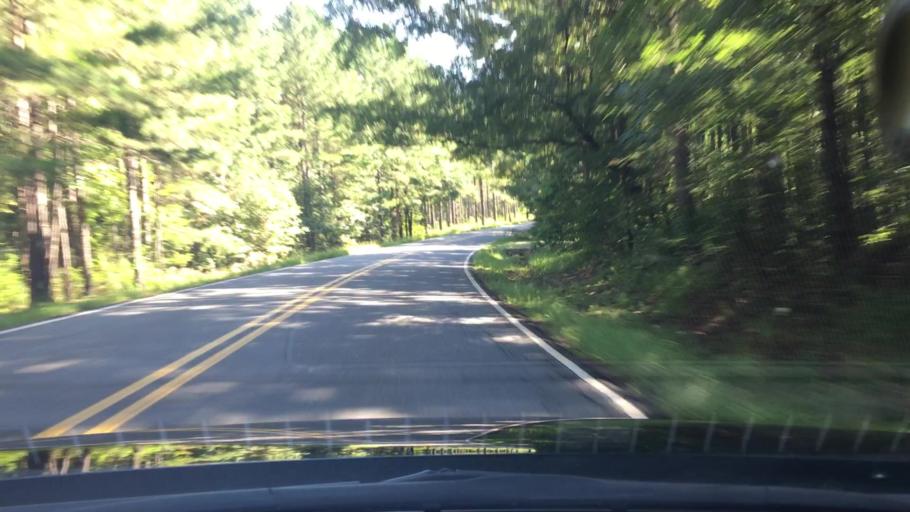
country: US
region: Georgia
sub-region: Putnam County
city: Jefferson
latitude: 33.4329
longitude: -83.3710
